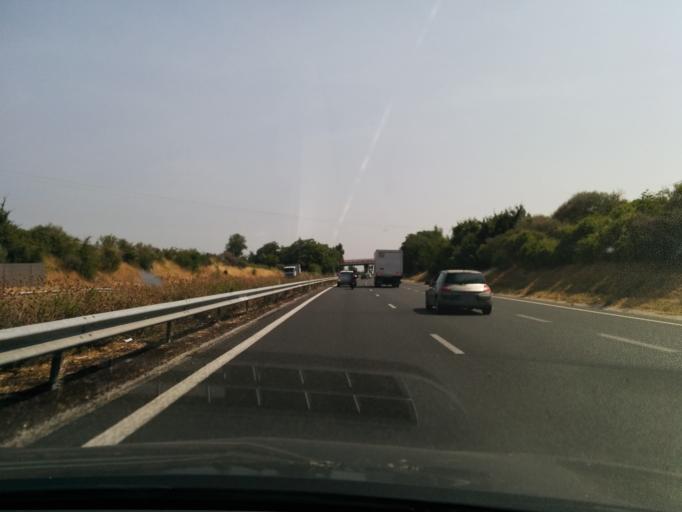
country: FR
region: Midi-Pyrenees
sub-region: Departement du Tarn
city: Brens
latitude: 43.8790
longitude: 1.9090
